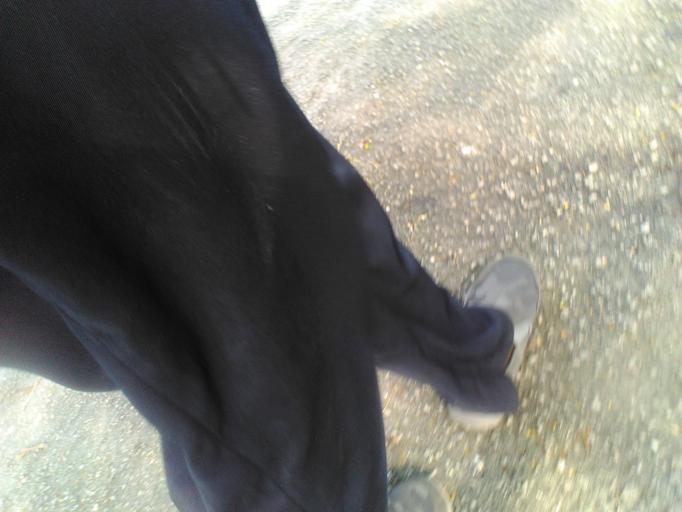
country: MY
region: Kedah
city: Kulim
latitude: 5.3711
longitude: 100.5413
